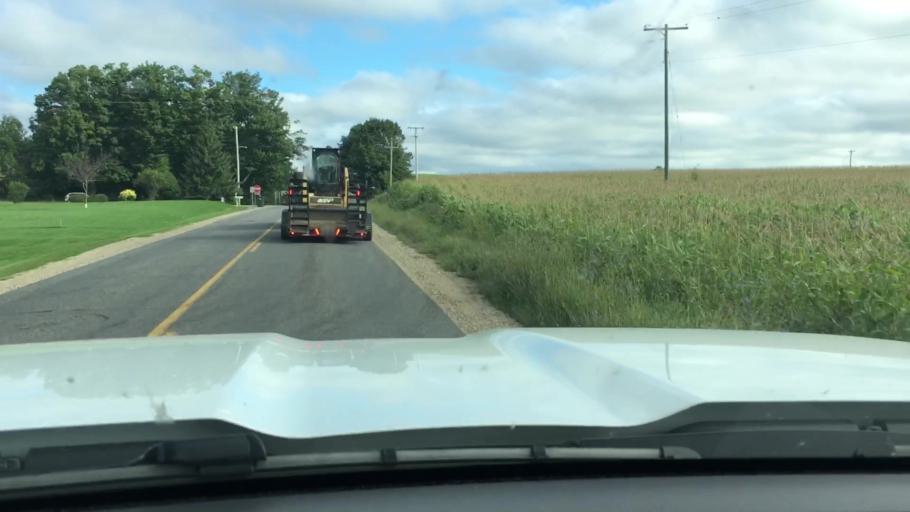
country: US
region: Michigan
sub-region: Kent County
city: Byron Center
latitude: 42.8103
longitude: -85.8026
